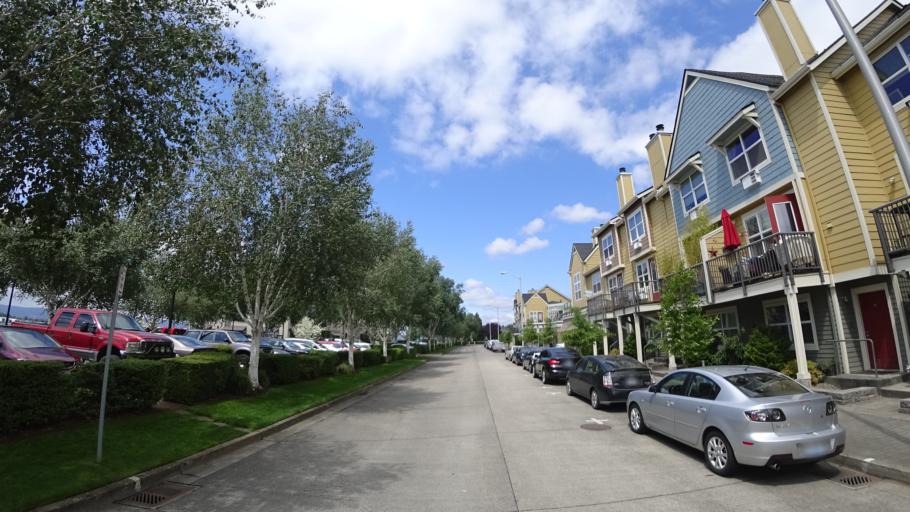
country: US
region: Washington
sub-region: Clark County
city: Vancouver
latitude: 45.6154
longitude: -122.6528
